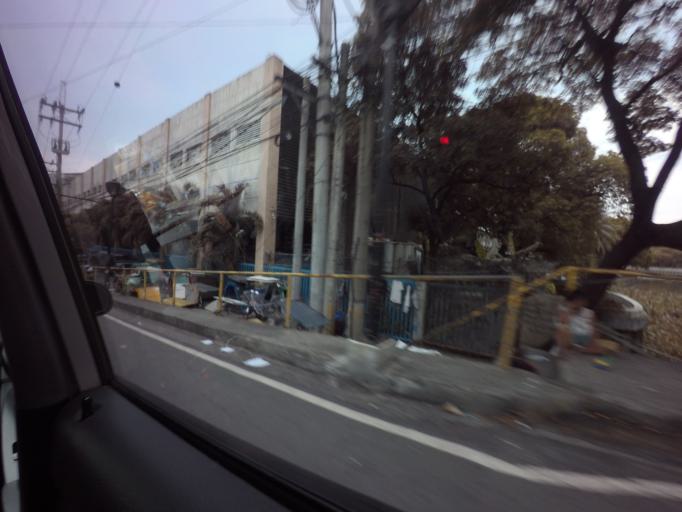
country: PH
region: Metro Manila
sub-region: City of Manila
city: Quiapo
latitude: 14.5952
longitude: 120.9840
